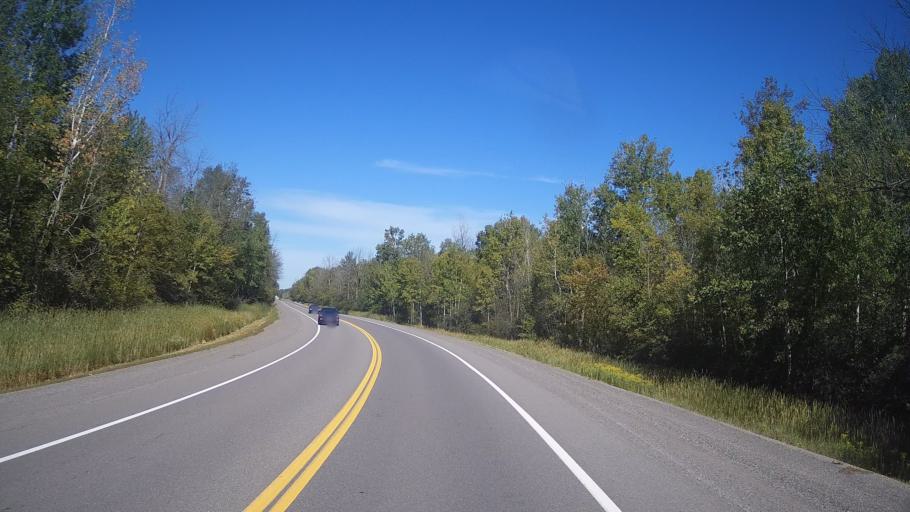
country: CA
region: Ontario
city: Bells Corners
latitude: 45.0776
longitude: -75.6488
